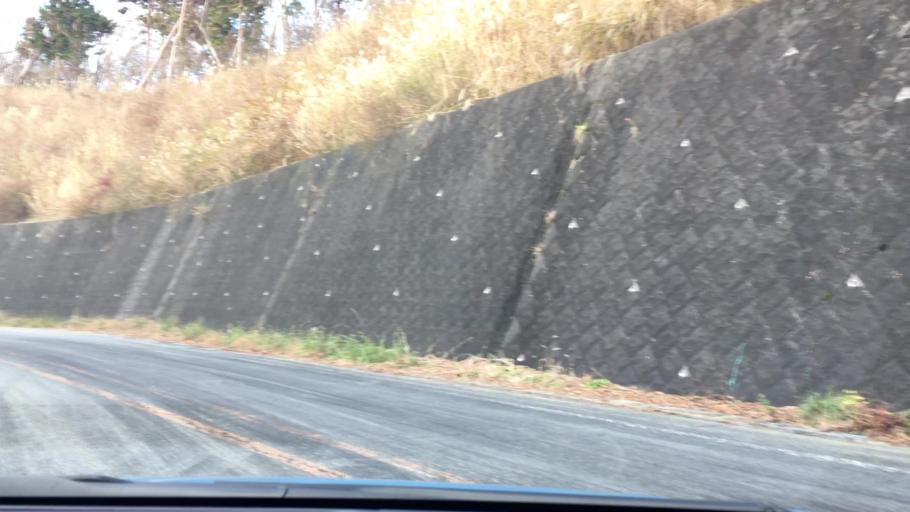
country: JP
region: Shizuoka
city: Gotemba
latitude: 35.4006
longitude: 138.9317
